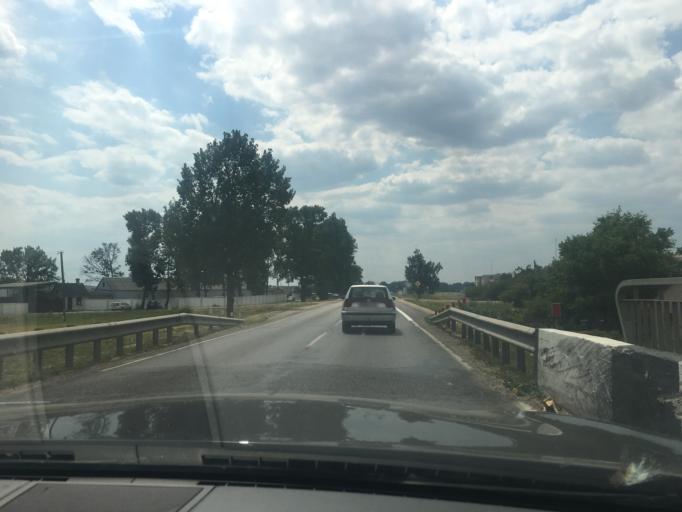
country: BY
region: Brest
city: Pruzhany
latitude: 52.5485
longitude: 24.4642
